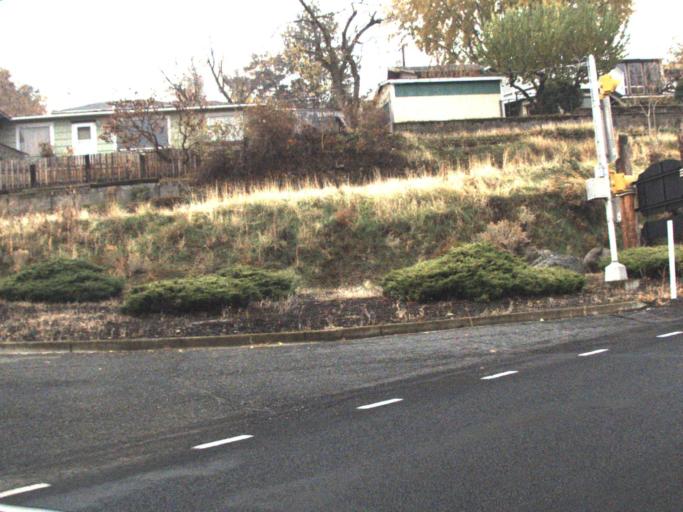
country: US
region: Washington
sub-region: Asotin County
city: Asotin
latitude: 46.3390
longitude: -117.0492
